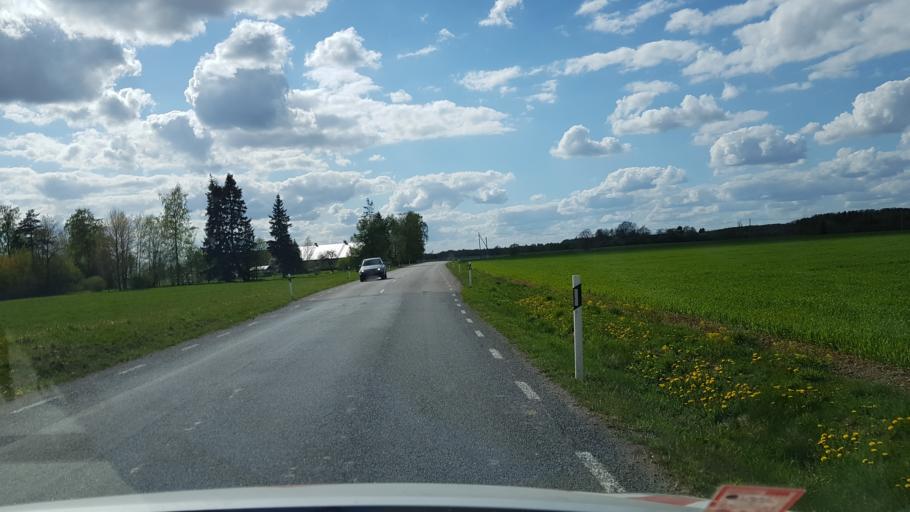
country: EE
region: Tartu
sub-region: Tartu linn
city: Tartu
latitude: 58.3958
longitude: 26.8490
